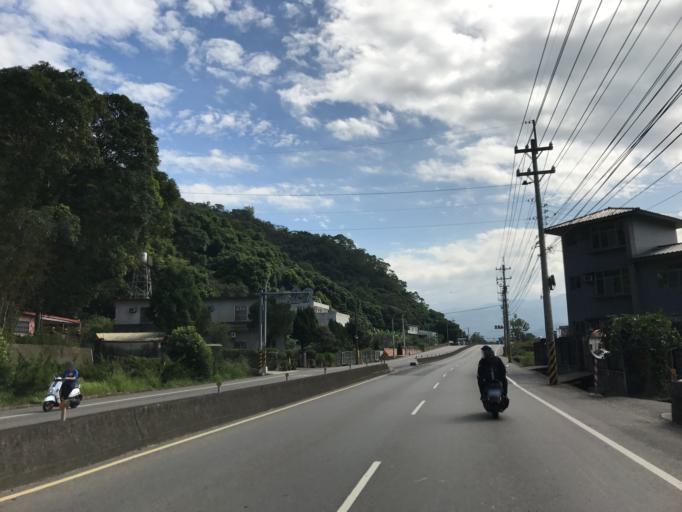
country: TW
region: Taiwan
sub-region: Hsinchu
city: Zhubei
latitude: 24.7410
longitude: 121.1092
